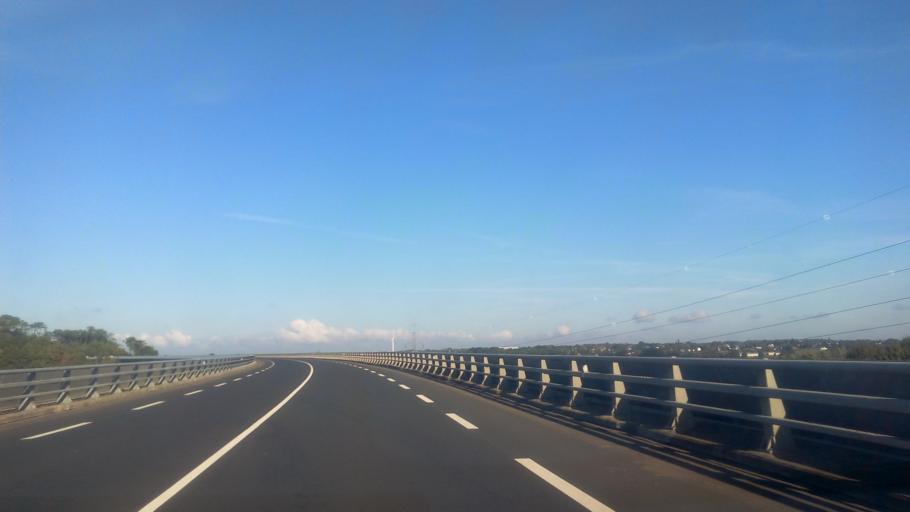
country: FR
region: Pays de la Loire
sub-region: Departement de la Loire-Atlantique
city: Saint-Nicolas-de-Redon
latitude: 47.6563
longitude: -2.0458
